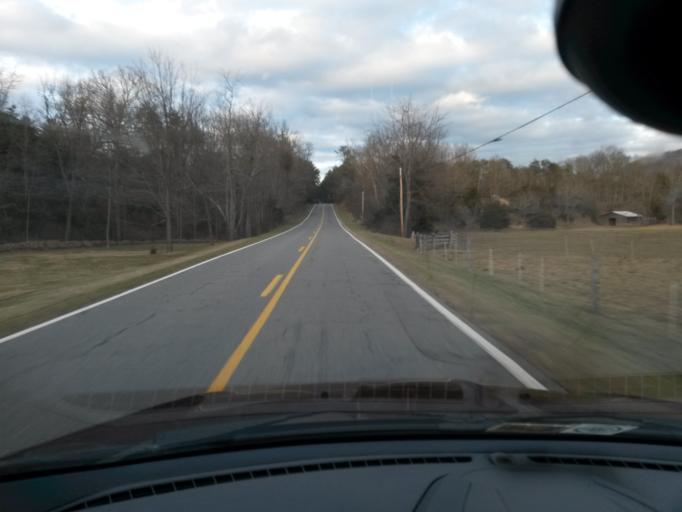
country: US
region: Virginia
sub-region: City of Covington
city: Covington
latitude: 37.7719
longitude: -80.1121
